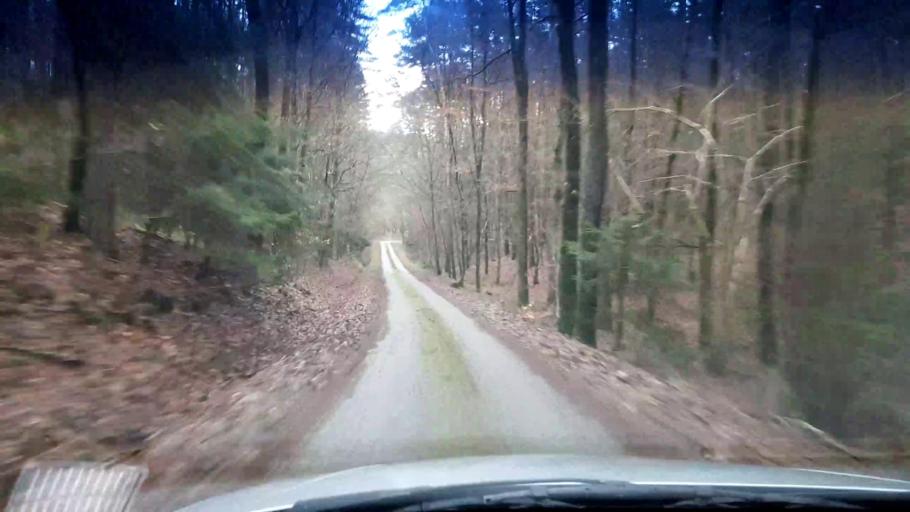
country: DE
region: Bavaria
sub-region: Upper Franconia
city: Lauter
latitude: 49.9444
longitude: 10.7845
